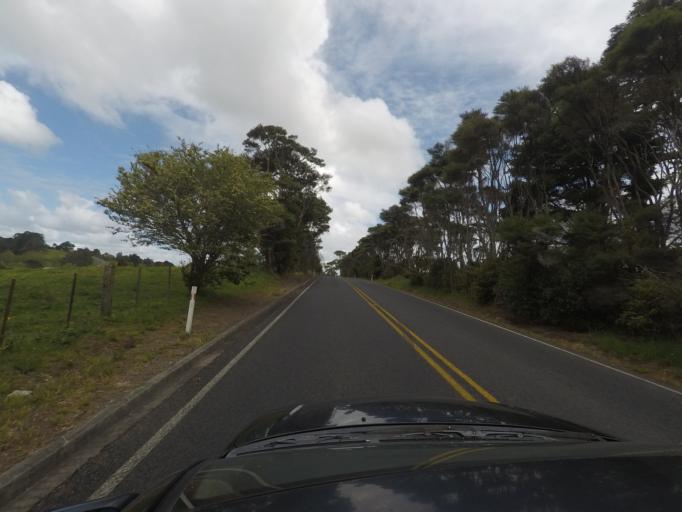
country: NZ
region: Auckland
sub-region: Auckland
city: Parakai
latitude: -36.6504
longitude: 174.5206
